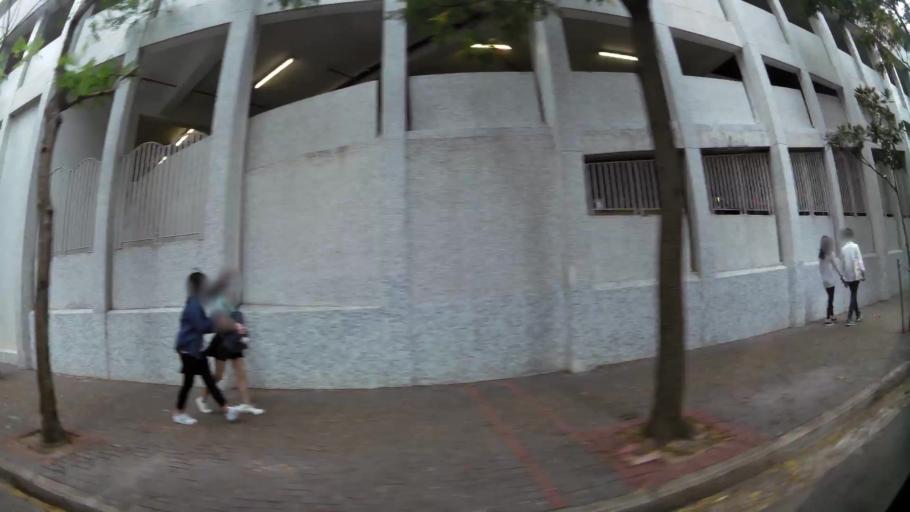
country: HK
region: Kowloon City
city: Kowloon
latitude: 22.3158
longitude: 114.1786
